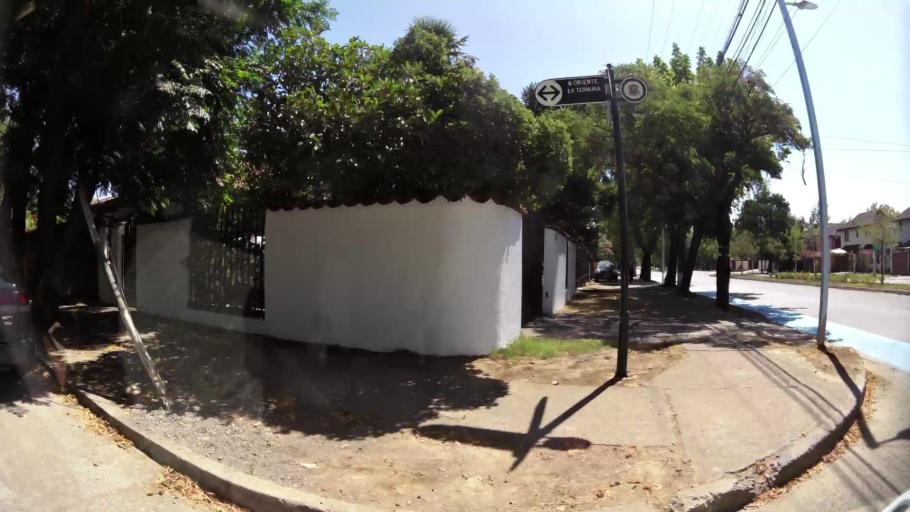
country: CL
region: Maule
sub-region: Provincia de Talca
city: Talca
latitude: -35.4128
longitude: -71.6540
